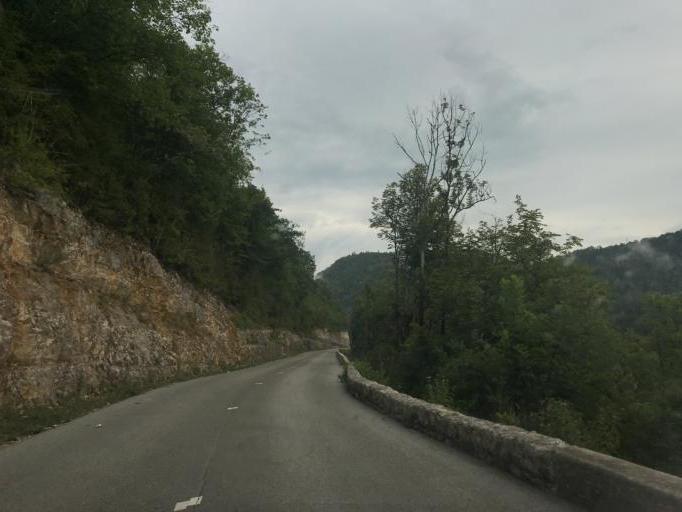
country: FR
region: Franche-Comte
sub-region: Departement du Jura
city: Lavans-les-Saint-Claude
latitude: 46.3351
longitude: 5.7645
